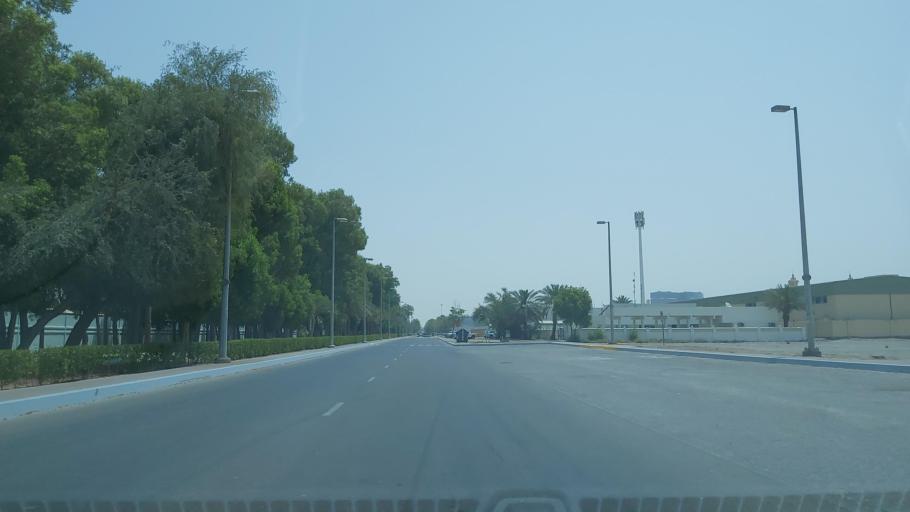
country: AE
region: Abu Dhabi
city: Abu Dhabi
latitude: 24.3792
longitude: 54.5171
